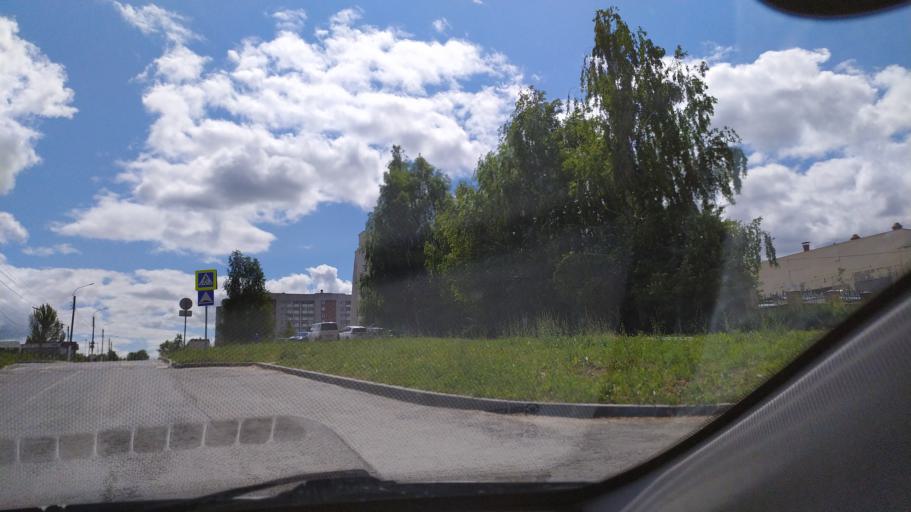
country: RU
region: Chuvashia
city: Novyye Lapsary
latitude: 56.1236
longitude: 47.1871
